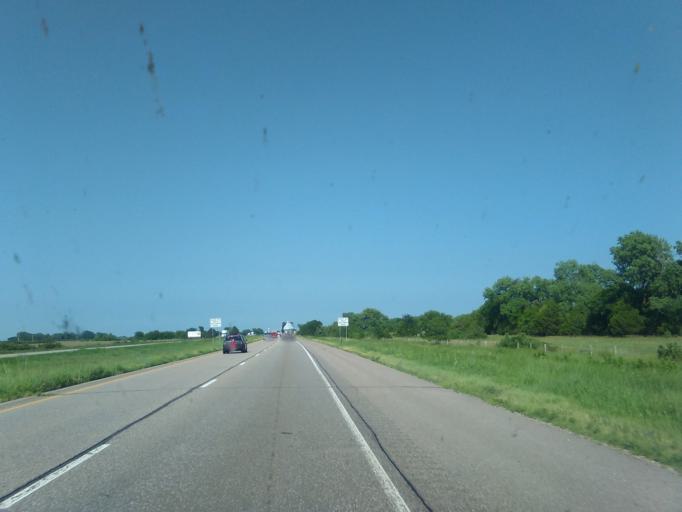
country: US
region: Nebraska
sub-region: Hall County
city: Grand Island
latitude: 40.8122
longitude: -98.4421
